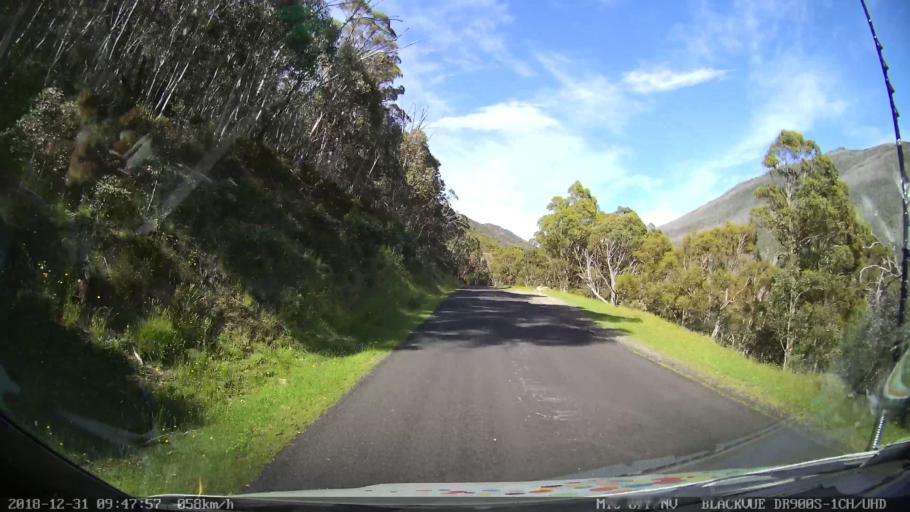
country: AU
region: New South Wales
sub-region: Snowy River
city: Jindabyne
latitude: -36.5106
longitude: 148.2974
